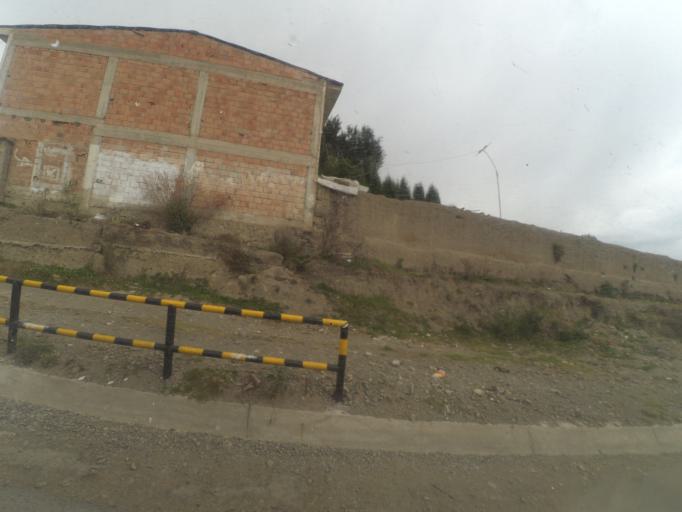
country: BO
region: La Paz
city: La Paz
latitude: -16.5701
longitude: -68.1749
